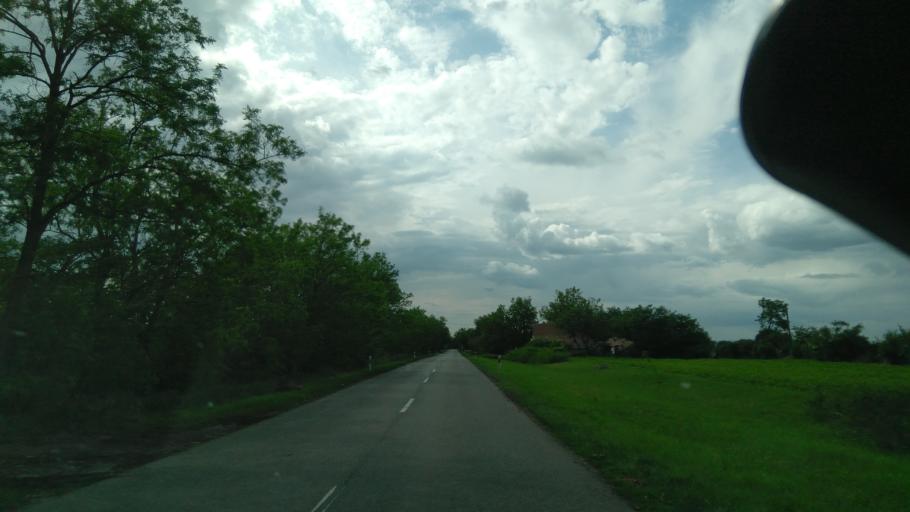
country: HU
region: Bekes
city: Gadoros
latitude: 46.6207
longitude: 20.6127
